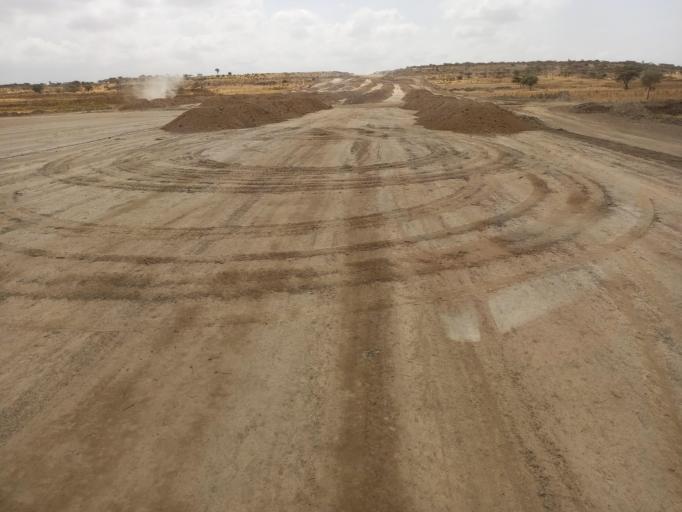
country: ET
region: Oromiya
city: Shashemene
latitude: 7.4889
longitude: 38.6807
